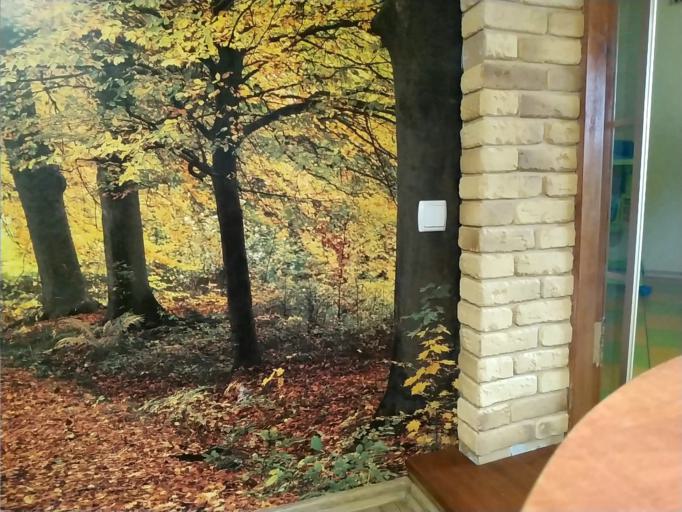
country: RU
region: Smolensk
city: Dorogobuzh
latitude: 54.8975
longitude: 33.3144
